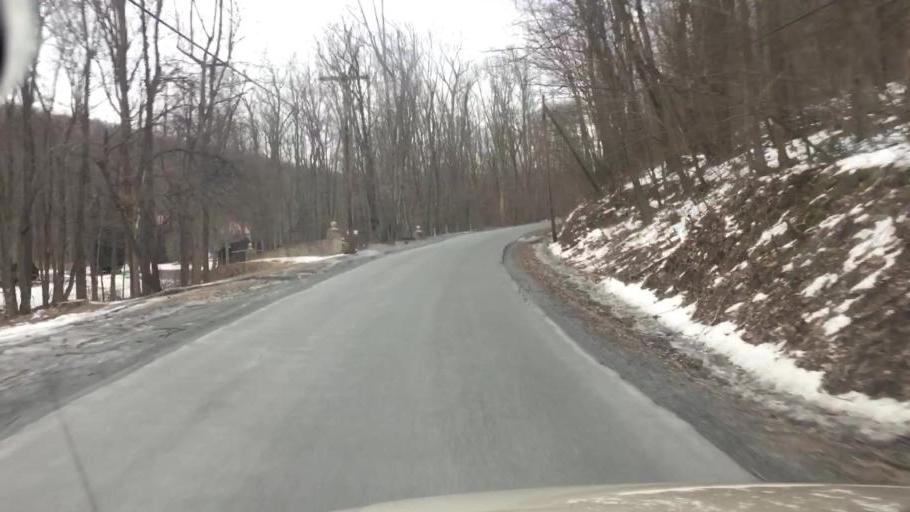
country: US
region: Pennsylvania
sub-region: Luzerne County
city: Oakdale
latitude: 41.0157
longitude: -75.9401
